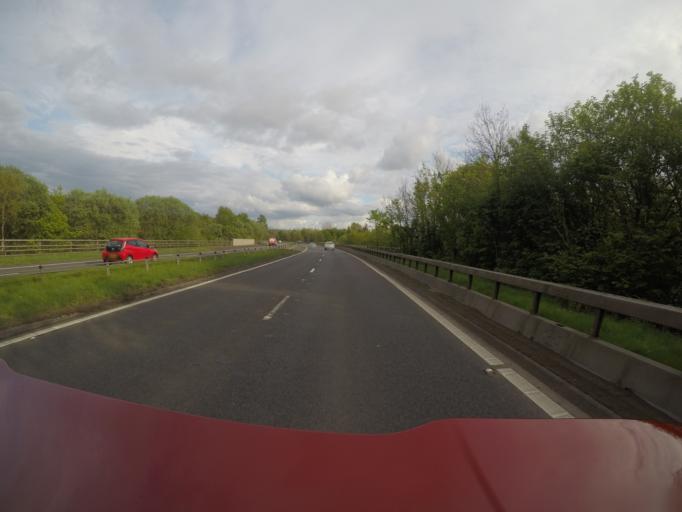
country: GB
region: Scotland
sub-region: West Dunbartonshire
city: Renton
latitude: 55.9635
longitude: -4.5865
